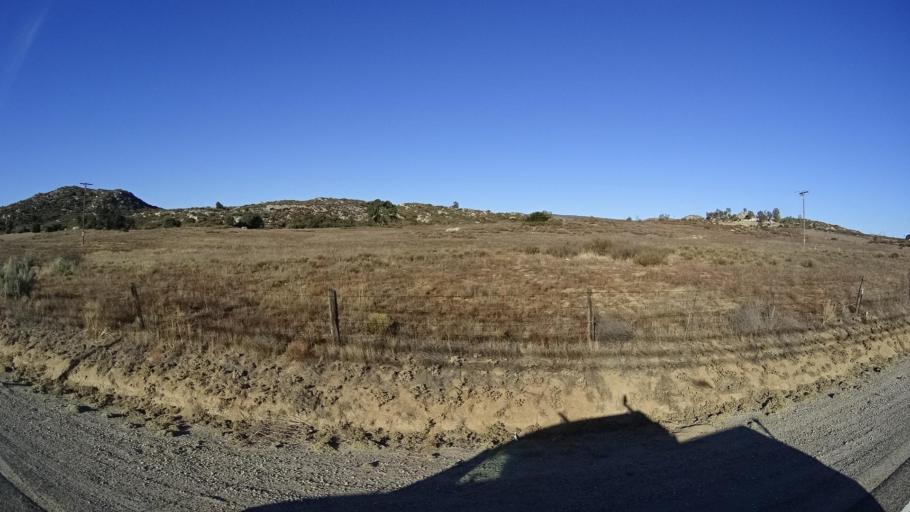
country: US
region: California
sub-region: San Diego County
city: Campo
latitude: 32.6185
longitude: -116.4759
